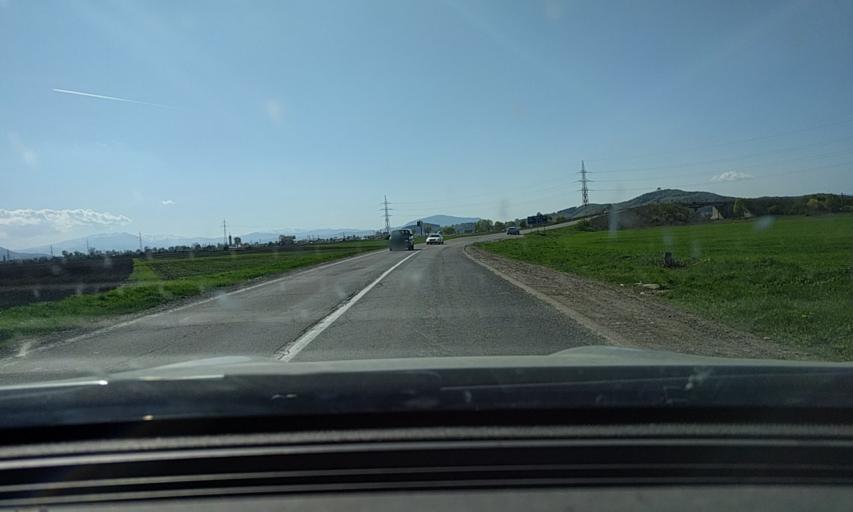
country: RO
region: Brasov
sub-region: Comuna Harman
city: Harman
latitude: 45.7098
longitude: 25.7110
